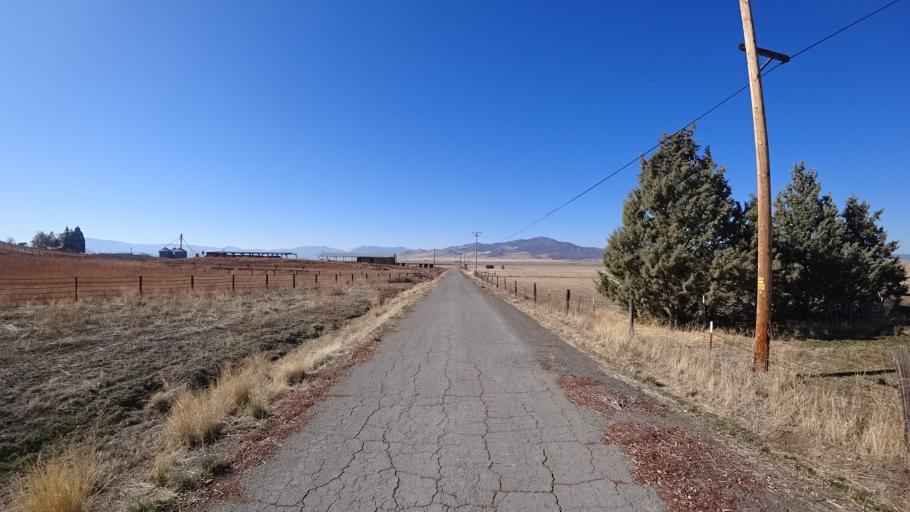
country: US
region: California
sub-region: Siskiyou County
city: Montague
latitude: 41.7937
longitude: -122.4309
